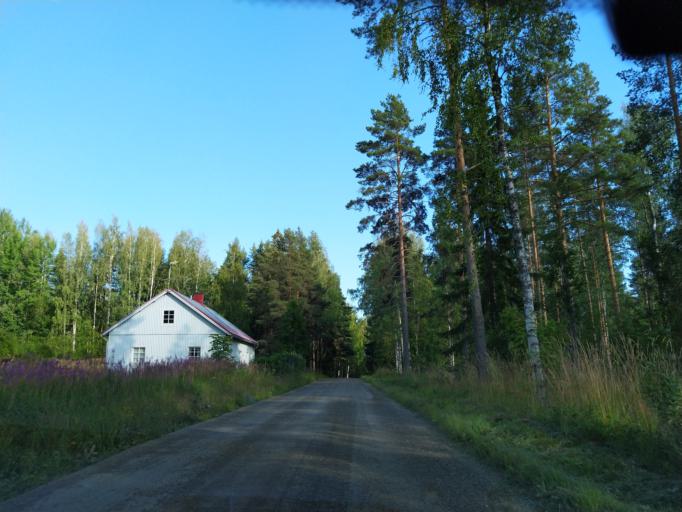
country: FI
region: Central Finland
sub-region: Jaemsae
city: Kuhmoinen
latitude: 61.6862
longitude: 24.9677
